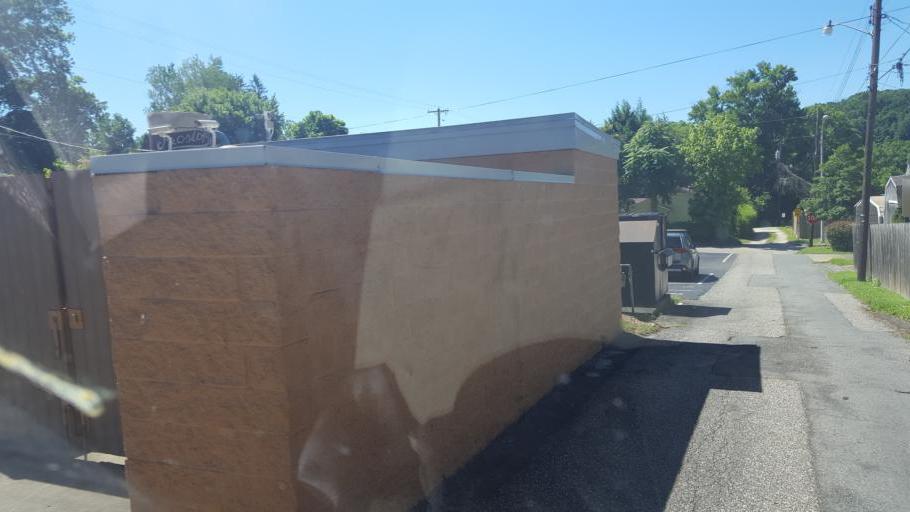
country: US
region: West Virginia
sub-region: Cabell County
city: Huntington
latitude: 38.4073
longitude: -82.4285
